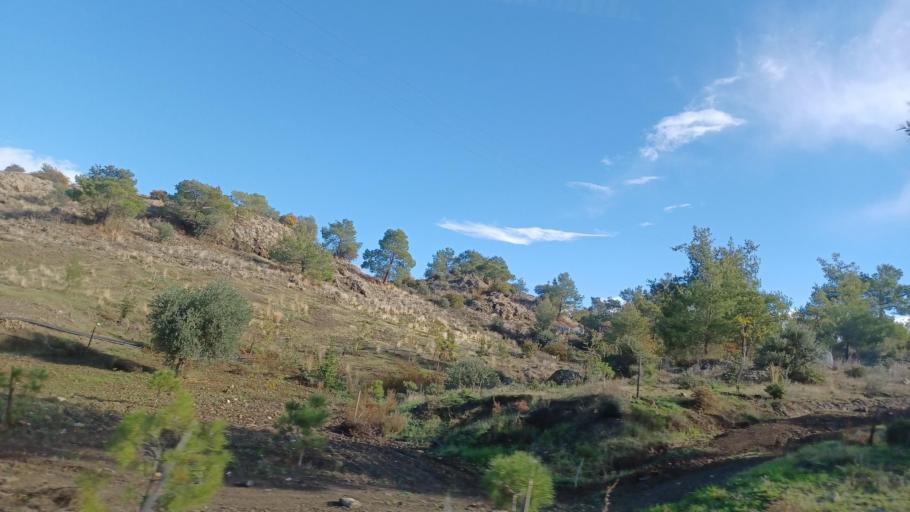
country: CY
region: Lefkosia
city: Lythrodontas
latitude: 34.9433
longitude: 33.2954
